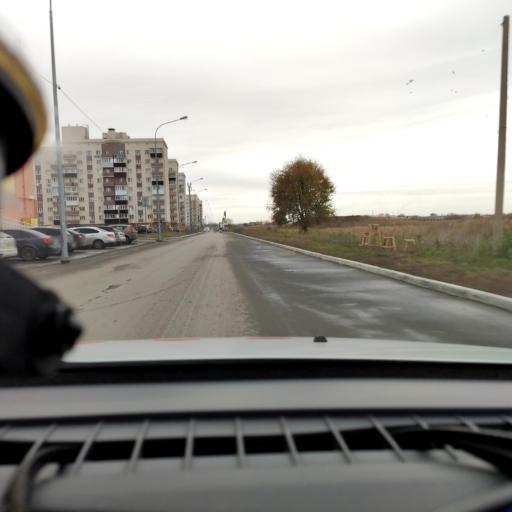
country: RU
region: Samara
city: Samara
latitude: 53.1161
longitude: 50.1497
